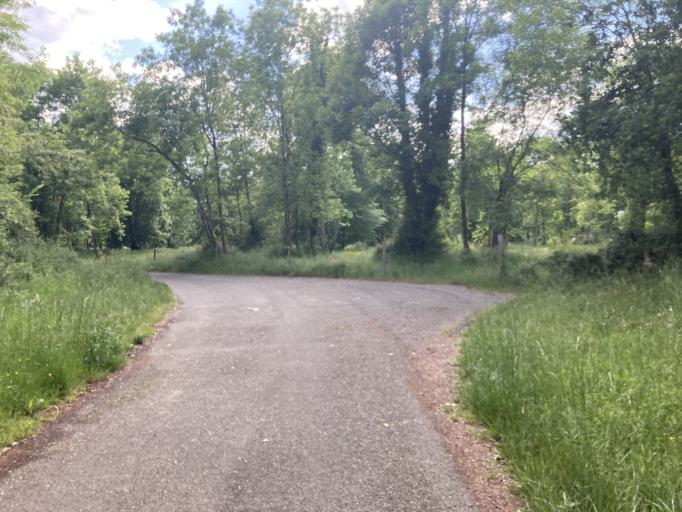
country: FR
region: Aquitaine
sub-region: Departement des Pyrenees-Atlantiques
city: Denguin
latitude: 43.3564
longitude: -0.5215
